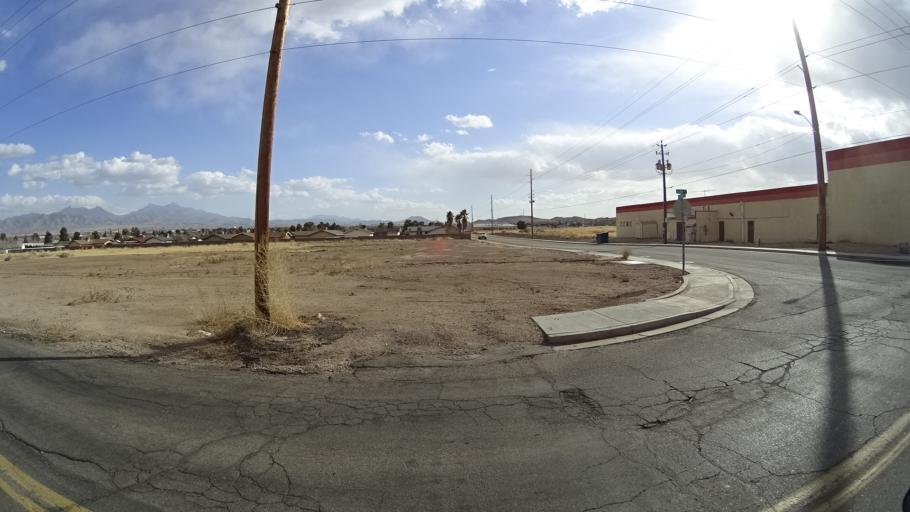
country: US
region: Arizona
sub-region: Mohave County
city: New Kingman-Butler
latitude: 35.2323
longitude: -114.0335
